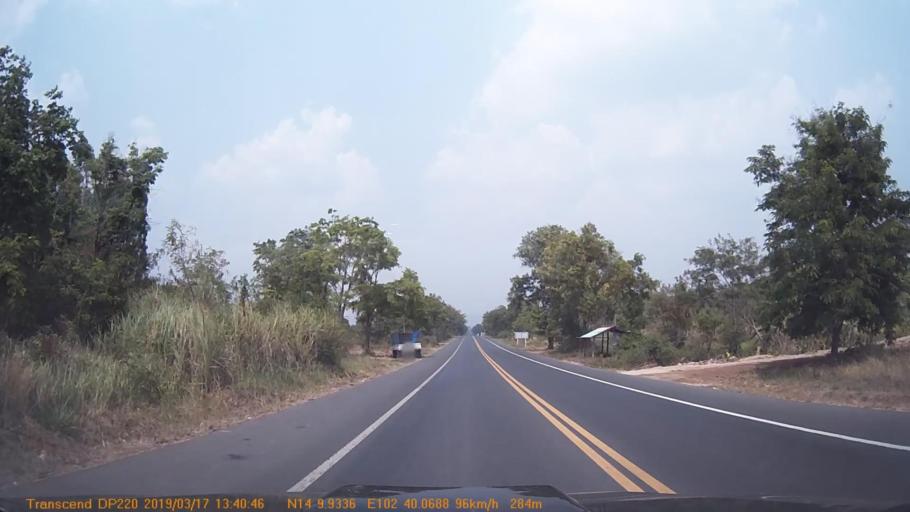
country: TH
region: Buriram
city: Non Din Daeng
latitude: 14.1658
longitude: 102.6680
